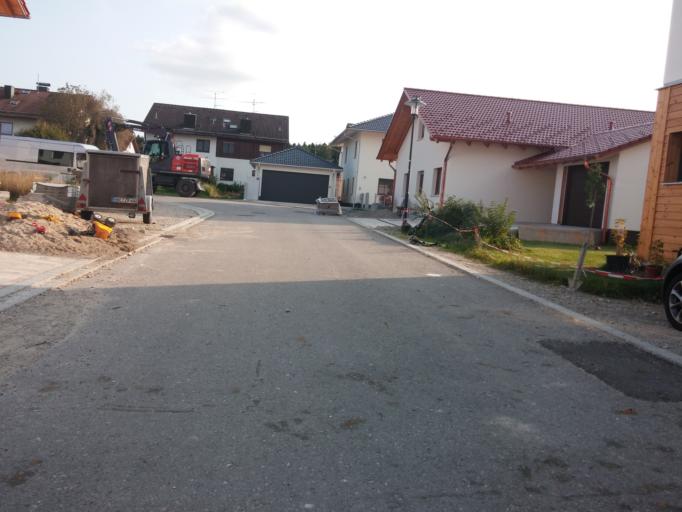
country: DE
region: Bavaria
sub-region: Upper Bavaria
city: Oberpframmern
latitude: 48.0210
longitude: 11.8026
